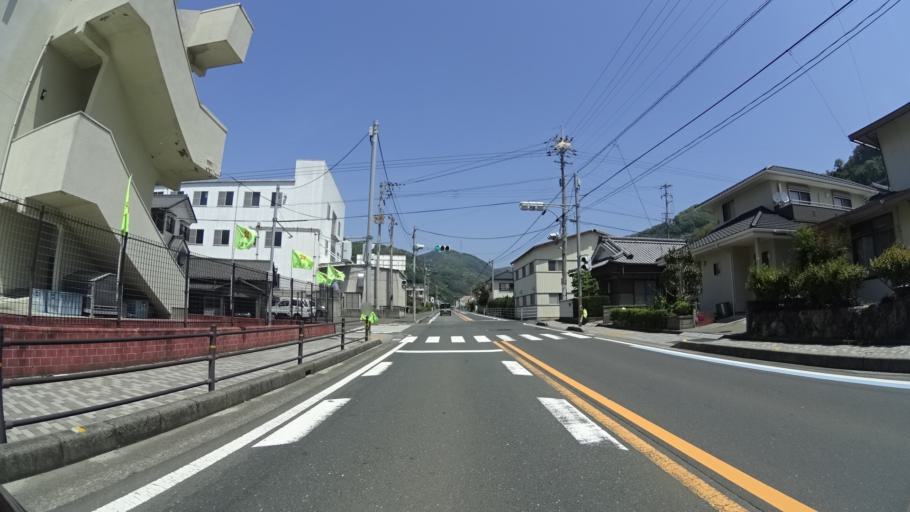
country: JP
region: Ehime
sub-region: Nishiuwa-gun
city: Ikata-cho
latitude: 33.4918
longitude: 132.3975
